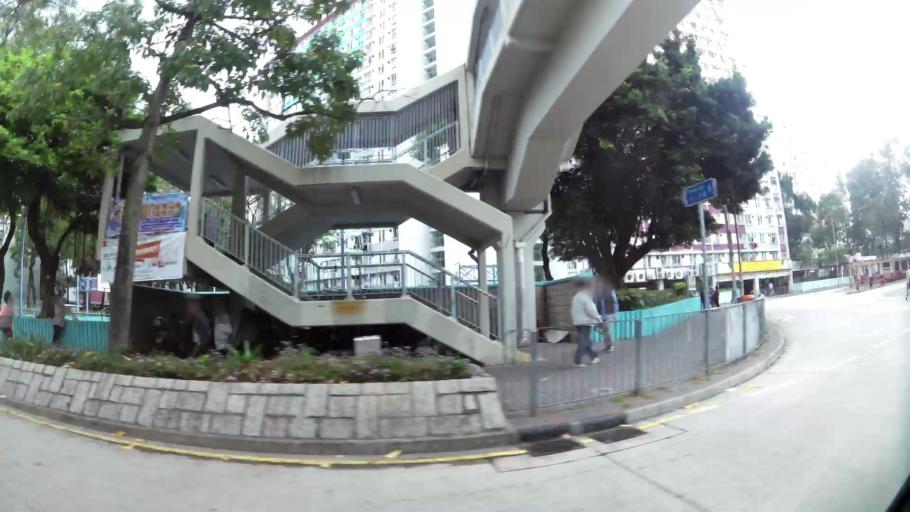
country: HK
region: Kowloon City
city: Kowloon
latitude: 22.3291
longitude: 114.2084
